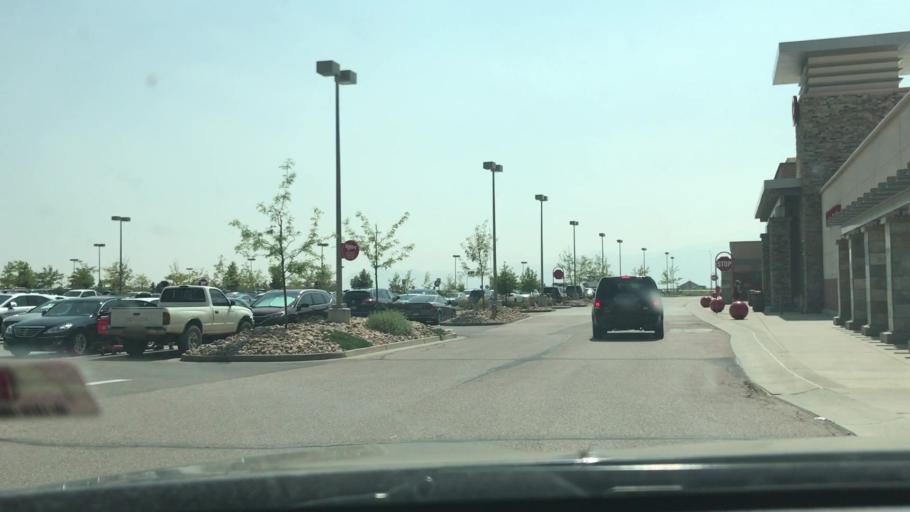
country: US
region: Colorado
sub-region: El Paso County
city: Black Forest
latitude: 38.9738
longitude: -104.7453
